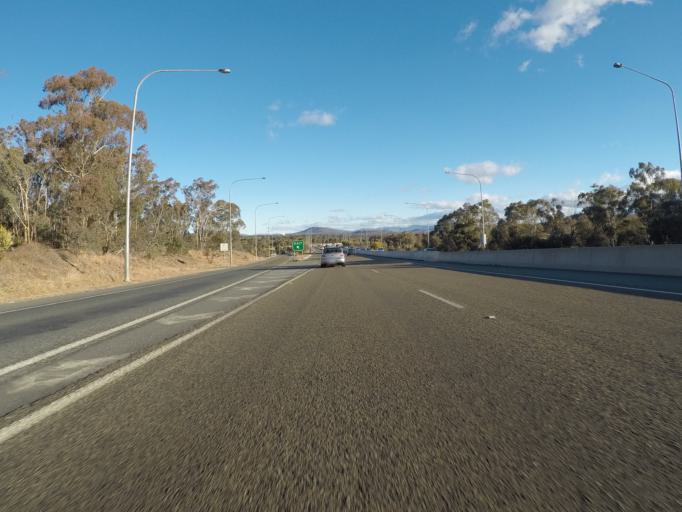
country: AU
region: Australian Capital Territory
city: Acton
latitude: -35.2782
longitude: 149.0868
